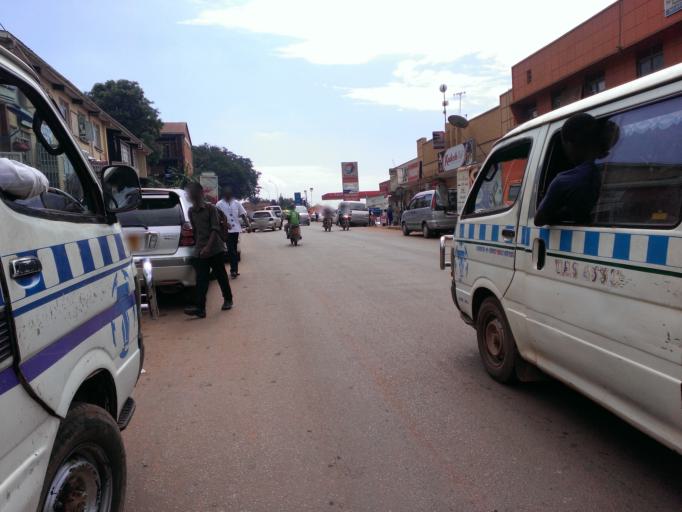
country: UG
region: Central Region
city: Kampala Central Division
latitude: 0.3111
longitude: 32.5588
